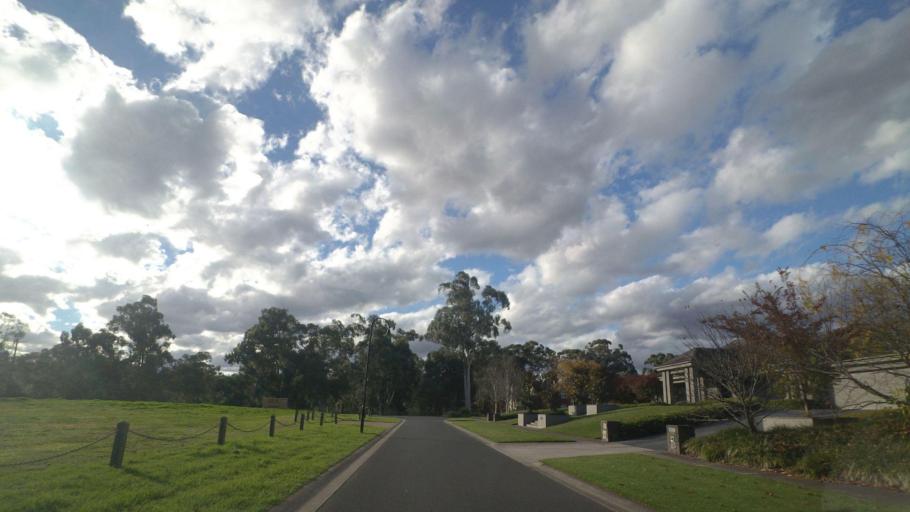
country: AU
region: Victoria
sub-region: Banyule
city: Lower Plenty
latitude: -37.7365
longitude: 145.1085
